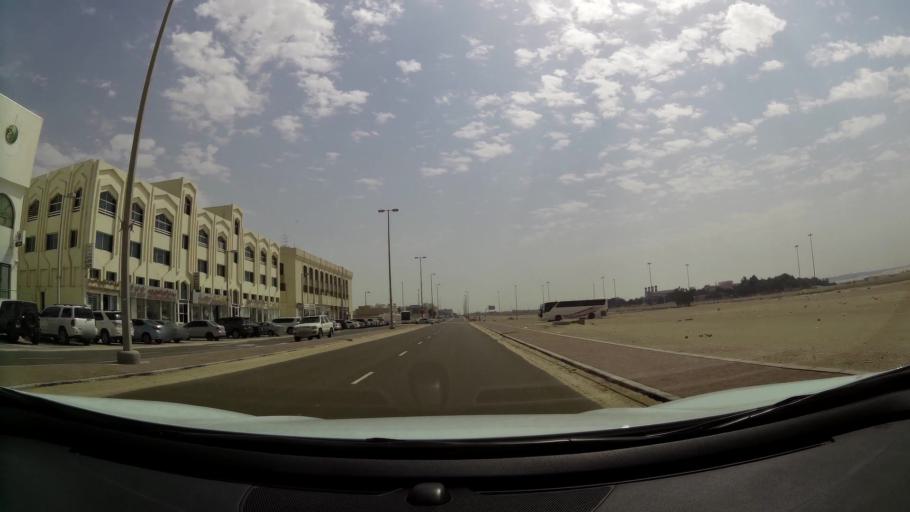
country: AE
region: Abu Dhabi
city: Abu Dhabi
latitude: 24.3088
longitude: 54.6078
